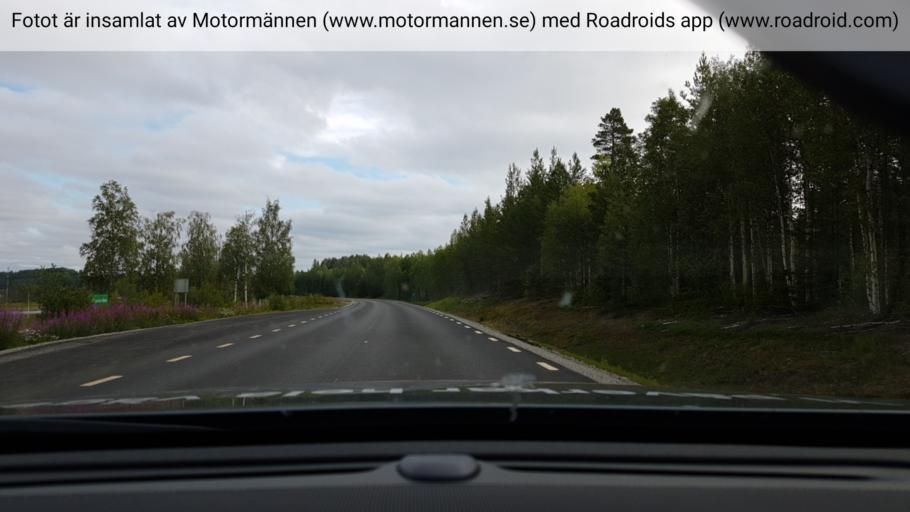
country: SE
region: Vaesterbotten
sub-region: Norsjo Kommun
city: Norsjoe
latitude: 64.5122
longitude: 19.3428
